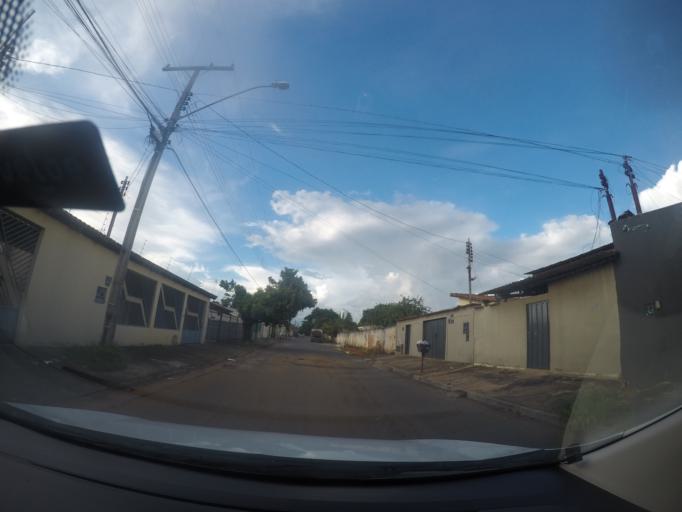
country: BR
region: Goias
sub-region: Goiania
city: Goiania
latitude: -16.6877
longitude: -49.3195
